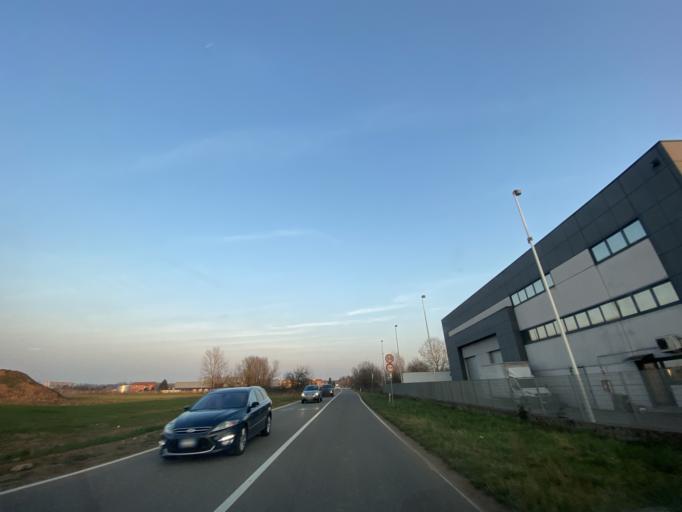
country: IT
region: Lombardy
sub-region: Citta metropolitana di Milano
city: Cesate
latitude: 45.6023
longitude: 9.0712
